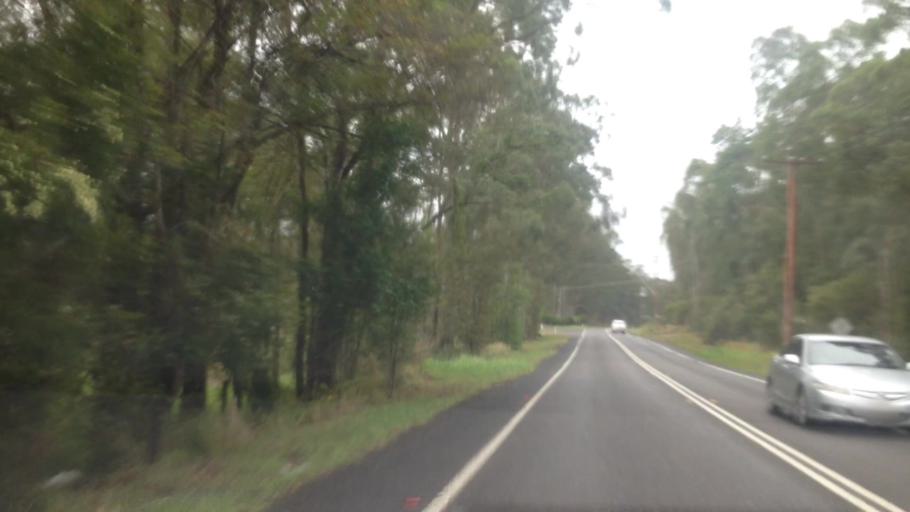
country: AU
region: New South Wales
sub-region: Wyong Shire
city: Little Jilliby
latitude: -33.2586
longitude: 151.3977
